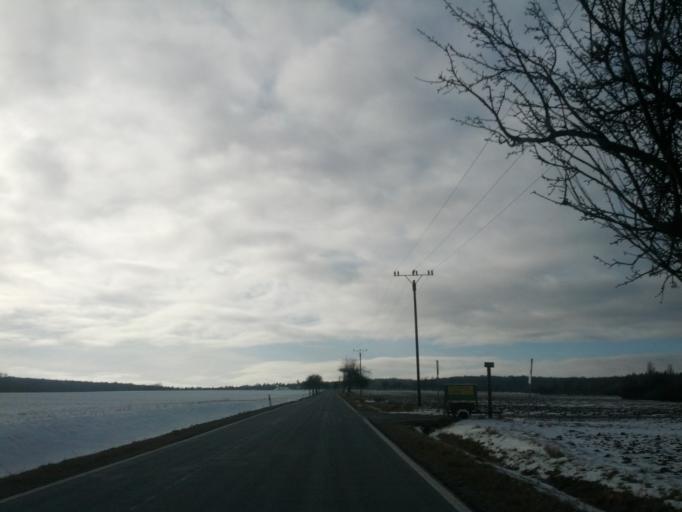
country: DE
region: Thuringia
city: Schonstedt
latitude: 51.0877
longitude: 10.5498
